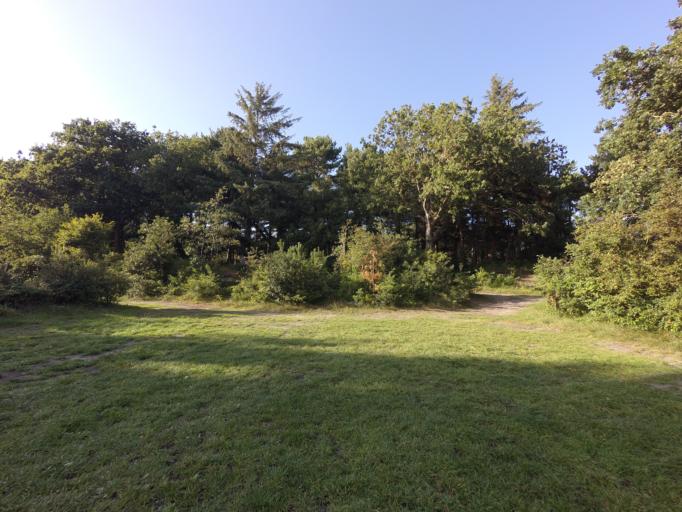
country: NL
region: Friesland
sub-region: Gemeente Terschelling
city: West-Terschelling
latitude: 53.3706
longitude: 5.2157
